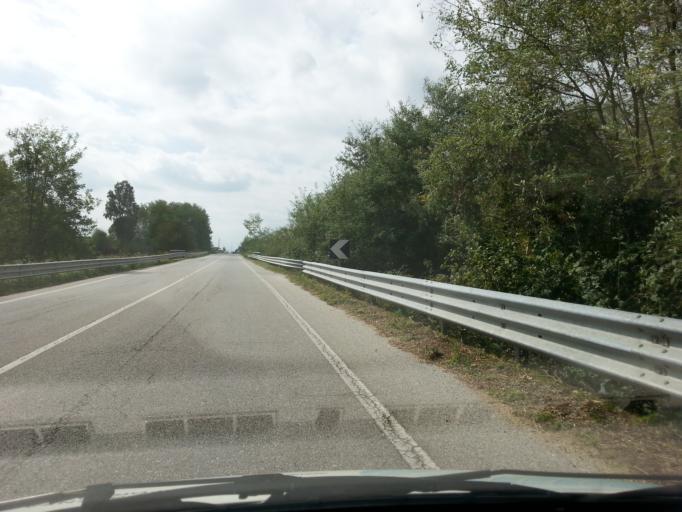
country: IT
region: Piedmont
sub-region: Provincia di Torino
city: Frossasco
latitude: 44.9386
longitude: 7.3729
